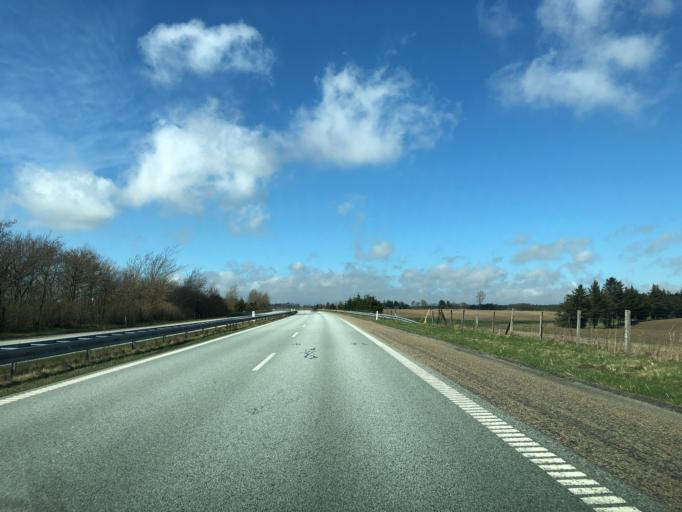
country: DK
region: North Denmark
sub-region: Hjorring Kommune
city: Hjorring
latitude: 57.4867
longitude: 10.0302
